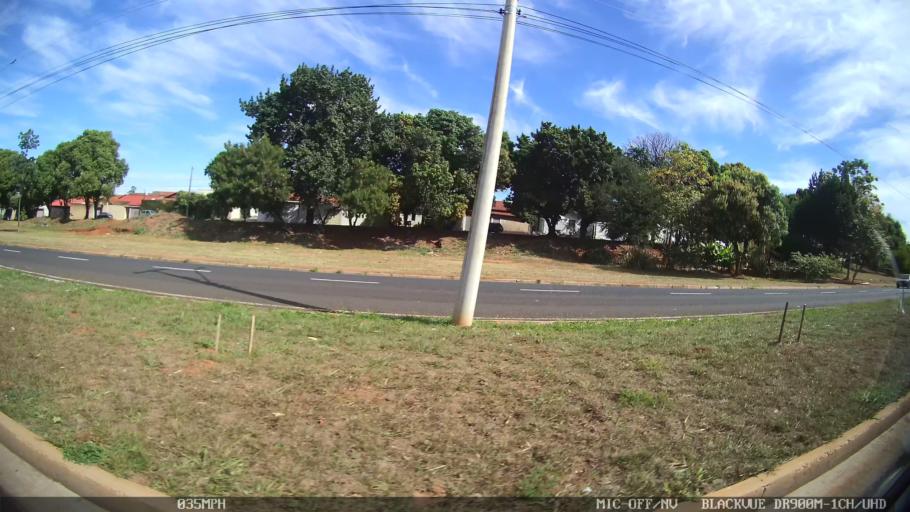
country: BR
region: Sao Paulo
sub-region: Sao Jose Do Rio Preto
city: Sao Jose do Rio Preto
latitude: -20.8353
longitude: -49.3467
